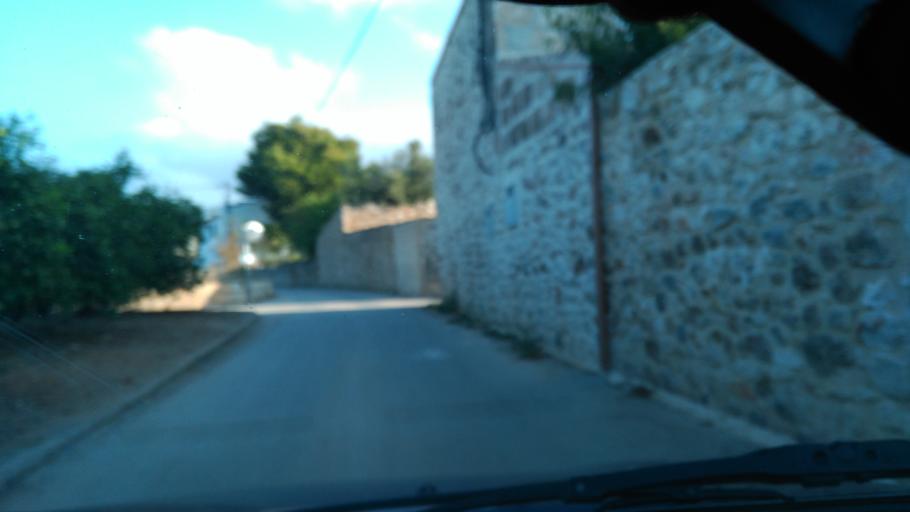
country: ES
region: Valencia
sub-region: Provincia de Alicante
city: Gata de Gorgos
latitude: 38.7838
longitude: 0.0895
